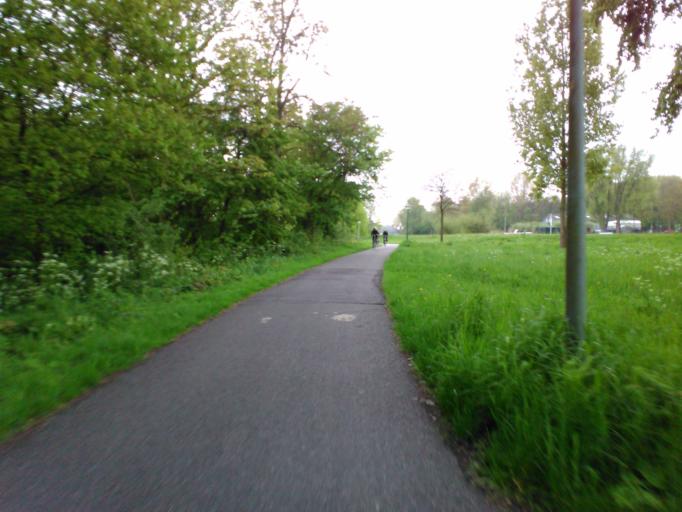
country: NL
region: South Holland
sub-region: Gemeente Vlaardingen
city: Vlaardingen
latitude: 51.9282
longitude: 4.3381
